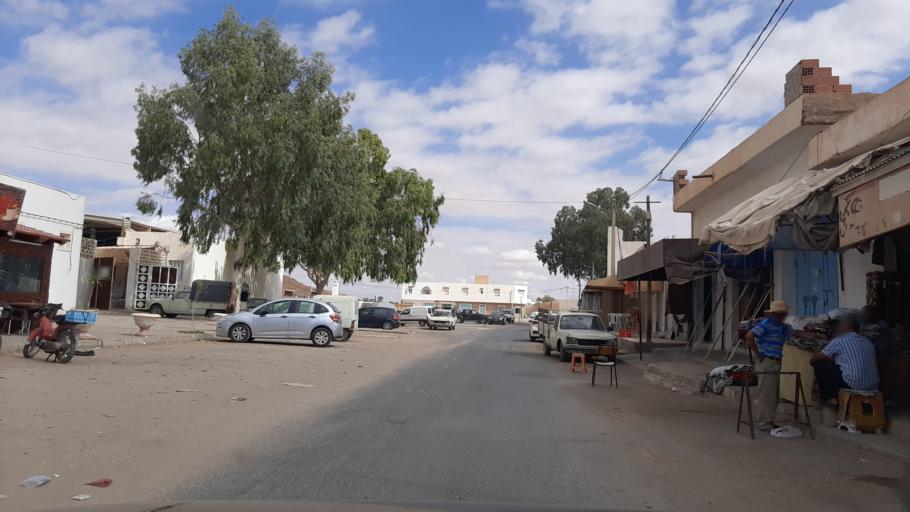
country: TN
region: Tataouine
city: Tataouine
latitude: 32.9263
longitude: 10.4407
